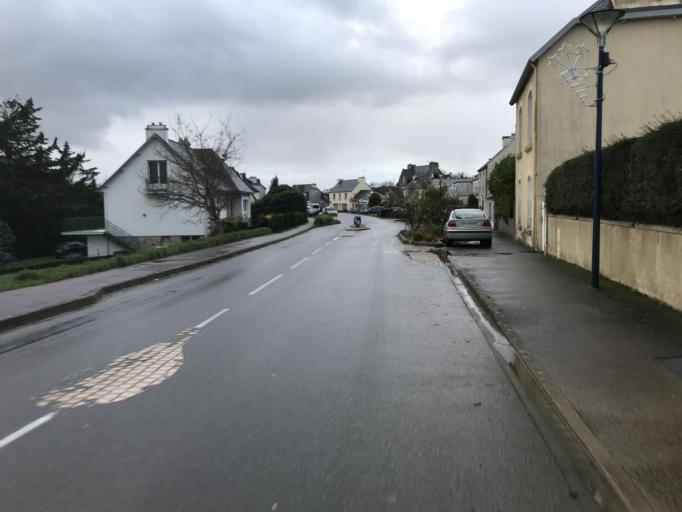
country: FR
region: Brittany
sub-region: Departement du Finistere
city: Loperhet
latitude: 48.3772
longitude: -4.3093
